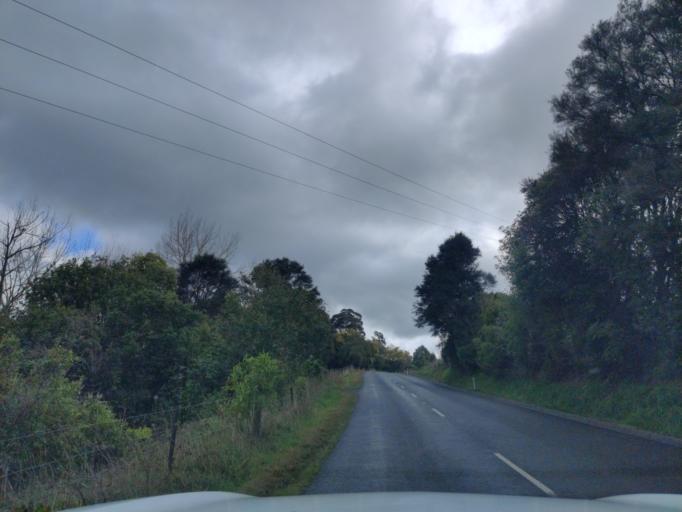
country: NZ
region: Manawatu-Wanganui
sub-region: Palmerston North City
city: Palmerston North
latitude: -40.1933
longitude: 175.7822
